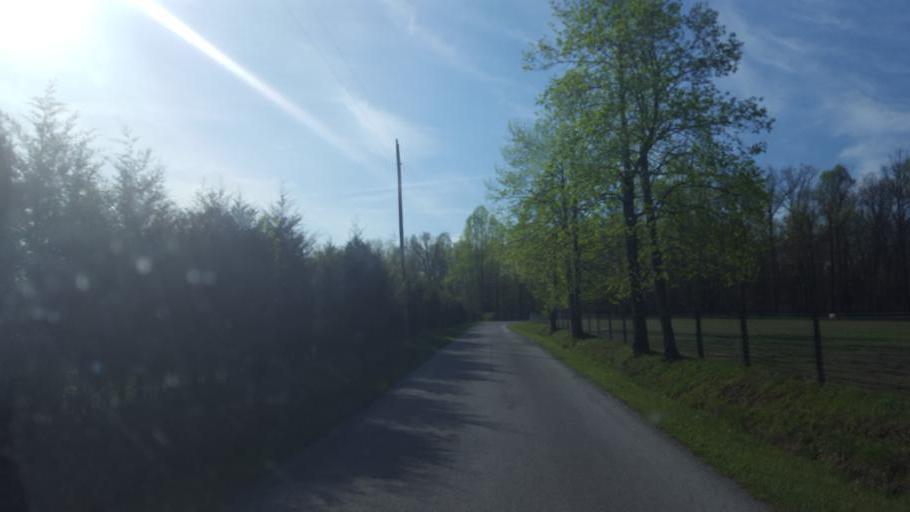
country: US
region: Kentucky
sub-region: Hart County
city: Munfordville
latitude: 37.3195
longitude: -86.0745
